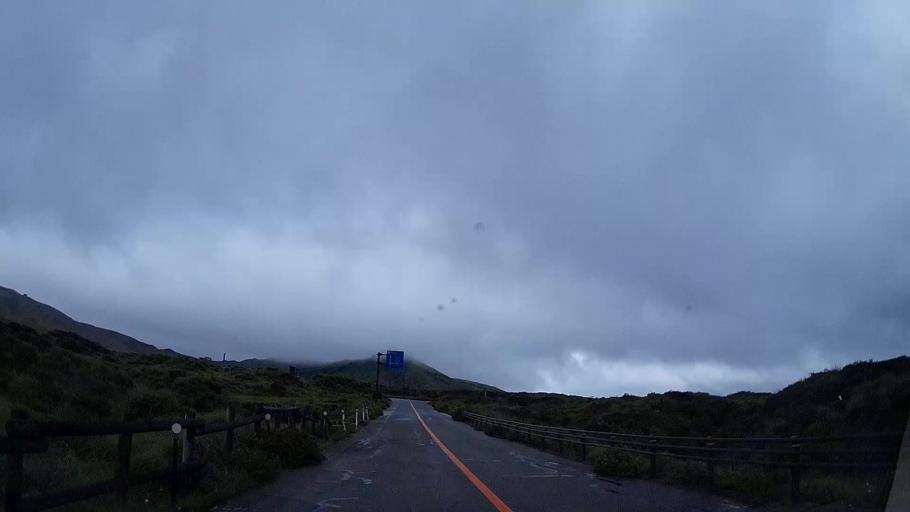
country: JP
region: Kumamoto
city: Aso
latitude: 32.8814
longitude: 131.0691
